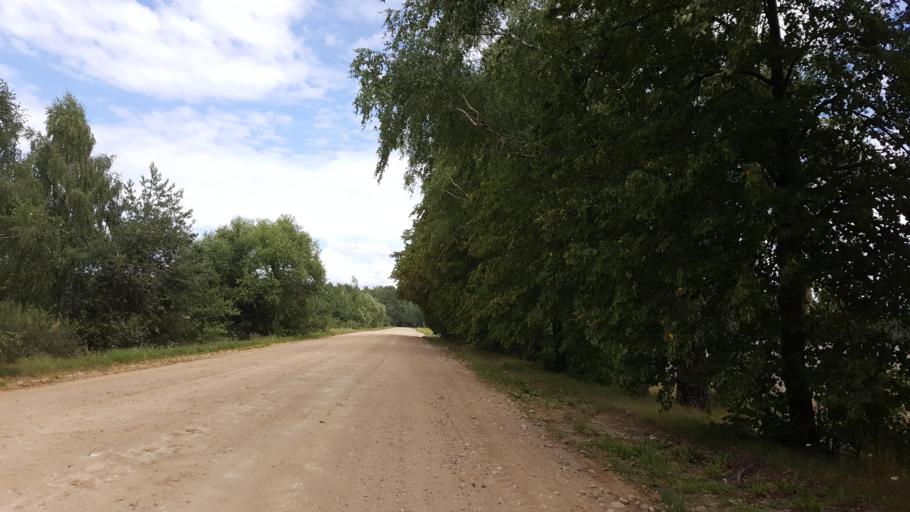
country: BY
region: Brest
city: Zhabinka
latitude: 52.2411
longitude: 24.0079
